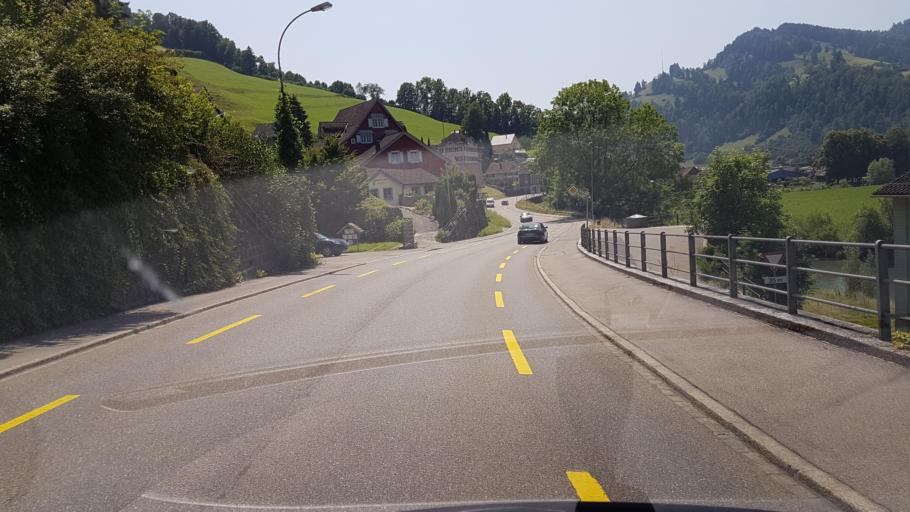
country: CH
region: Saint Gallen
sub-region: Wahlkreis Toggenburg
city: Lichtensteig
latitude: 47.3195
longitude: 9.0874
